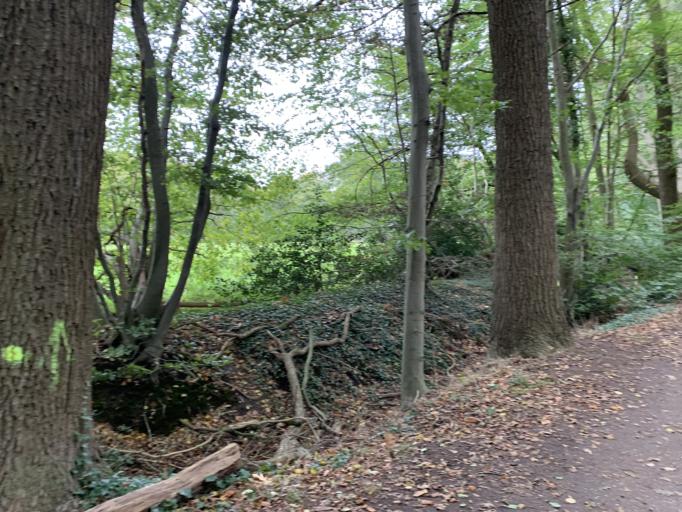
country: DE
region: North Rhine-Westphalia
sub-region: Regierungsbezirk Munster
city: Rheine
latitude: 52.2999
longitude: 7.4261
